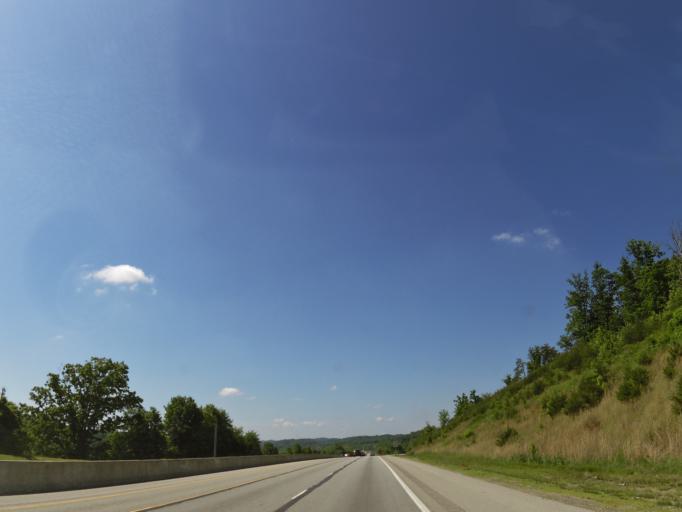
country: US
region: Kentucky
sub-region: Madison County
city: Berea
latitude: 37.4869
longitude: -84.3310
